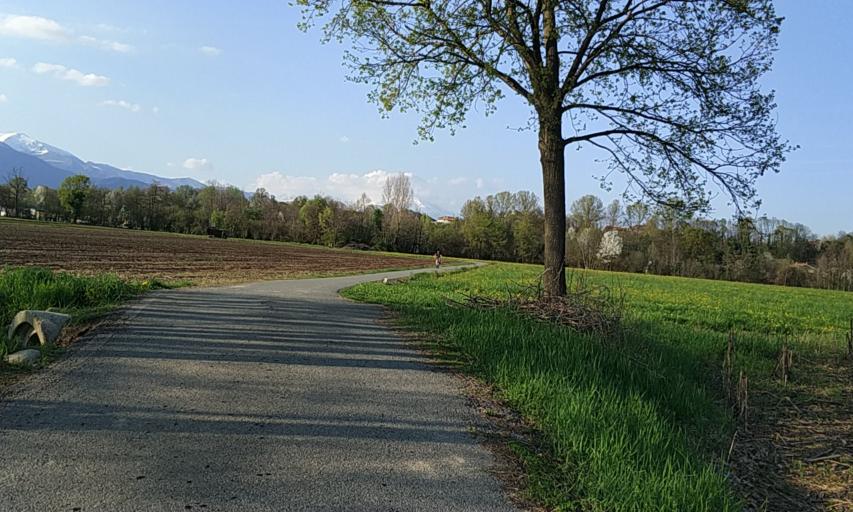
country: IT
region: Piedmont
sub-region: Provincia di Torino
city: San Carlo Canavese
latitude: 45.2439
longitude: 7.5918
